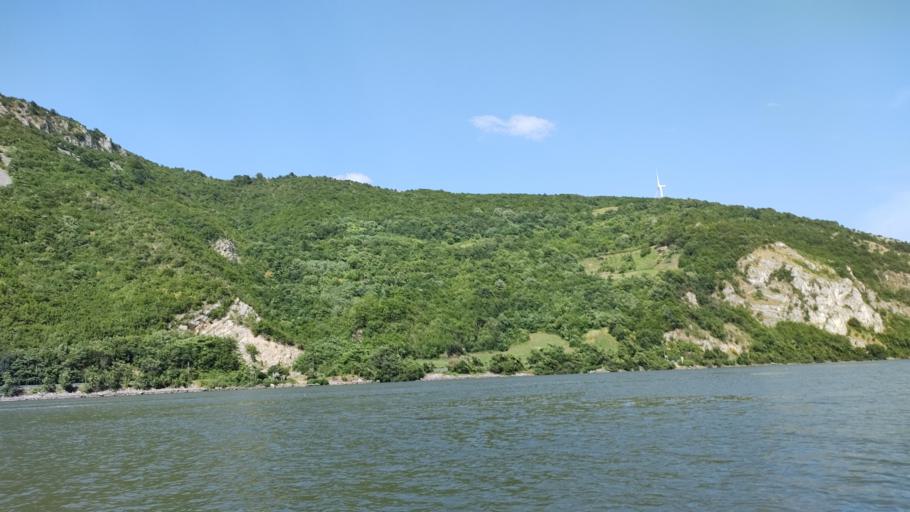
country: RO
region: Caras-Severin
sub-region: Comuna Pescari
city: Coronini
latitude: 44.6602
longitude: 21.7037
